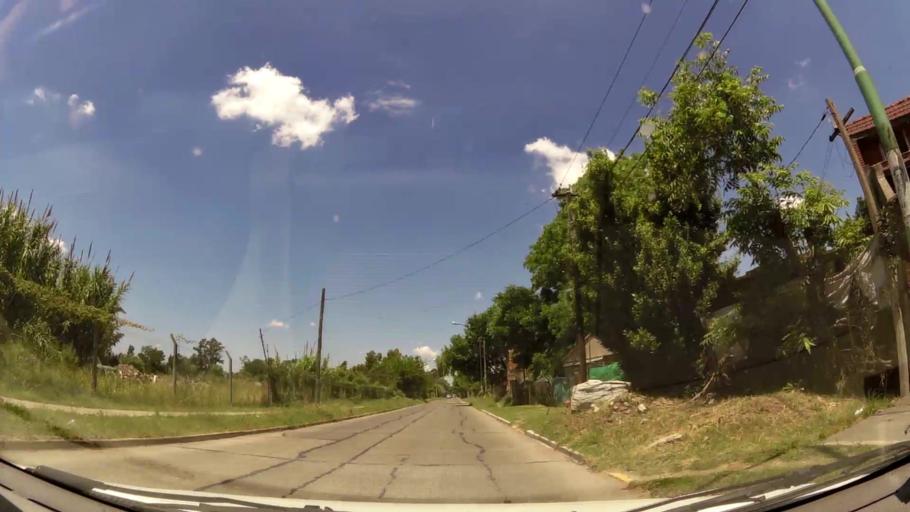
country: AR
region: Buenos Aires
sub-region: Partido de Merlo
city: Merlo
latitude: -34.6586
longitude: -58.7090
